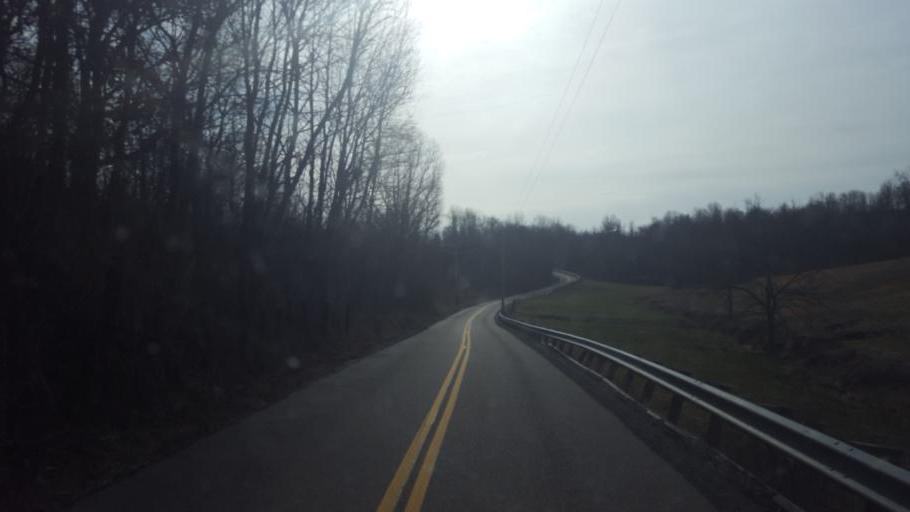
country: US
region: Ohio
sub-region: Gallia County
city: Gallipolis
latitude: 38.7142
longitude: -82.3442
